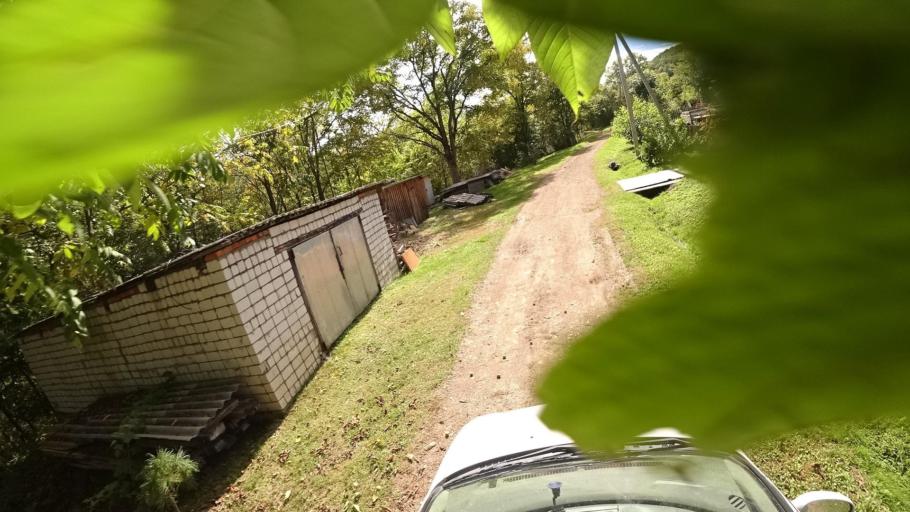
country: RU
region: Primorskiy
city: Yakovlevka
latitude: 44.3924
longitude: 133.6046
